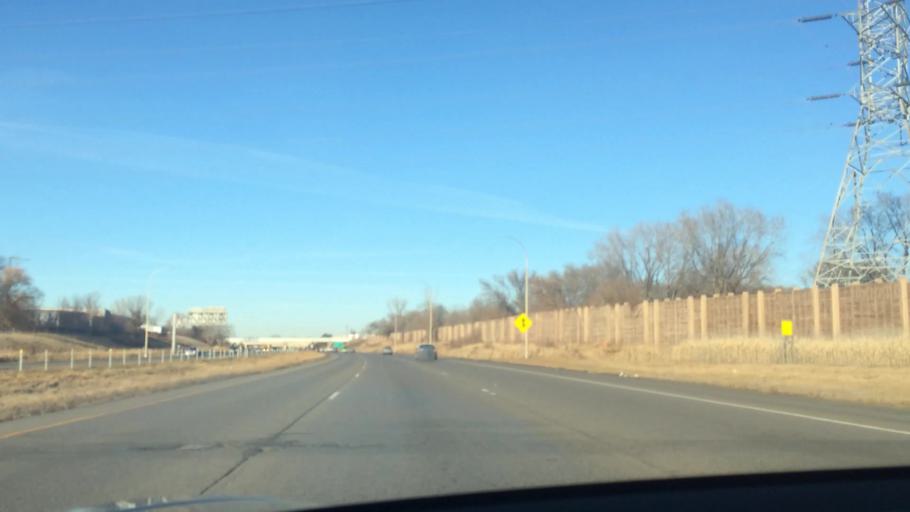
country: US
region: Minnesota
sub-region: Ramsey County
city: New Brighton
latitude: 45.0812
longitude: -93.1856
